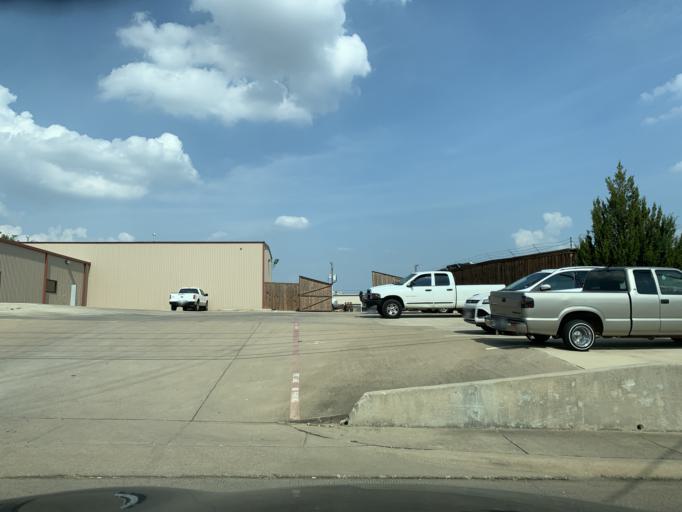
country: US
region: Texas
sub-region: Tarrant County
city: Richland Hills
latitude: 32.8077
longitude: -97.2211
